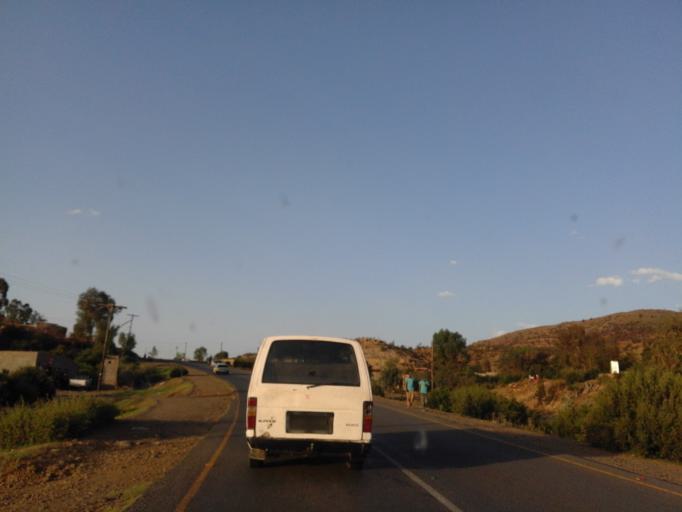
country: LS
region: Mafeteng
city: Mafeteng
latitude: -29.8393
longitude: 27.2326
